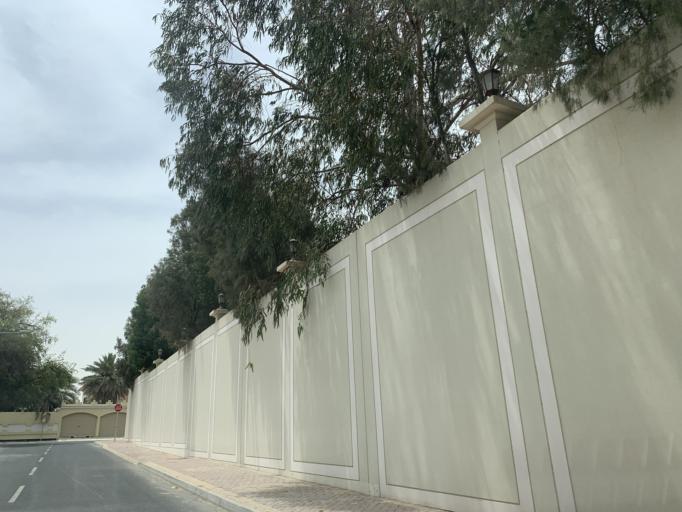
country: BH
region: Northern
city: Ar Rifa'
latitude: 26.1388
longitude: 50.5500
